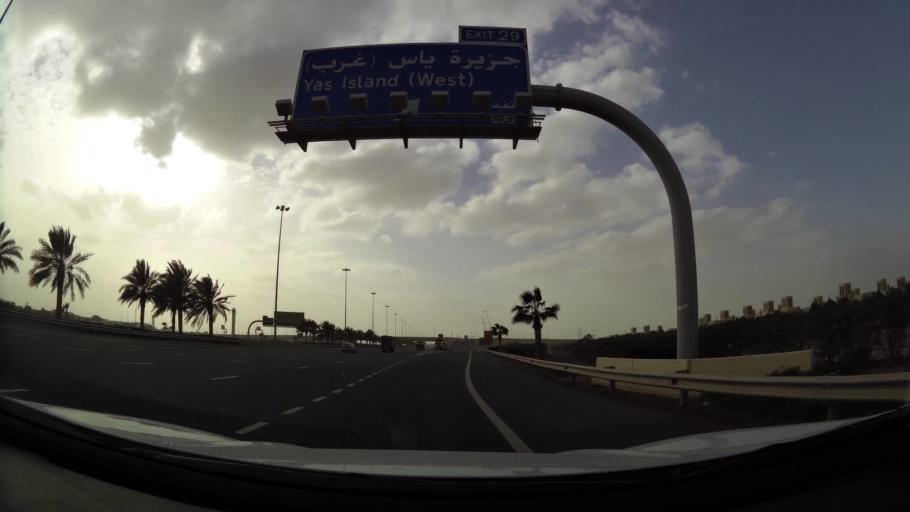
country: AE
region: Abu Dhabi
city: Abu Dhabi
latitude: 24.4991
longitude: 54.5966
